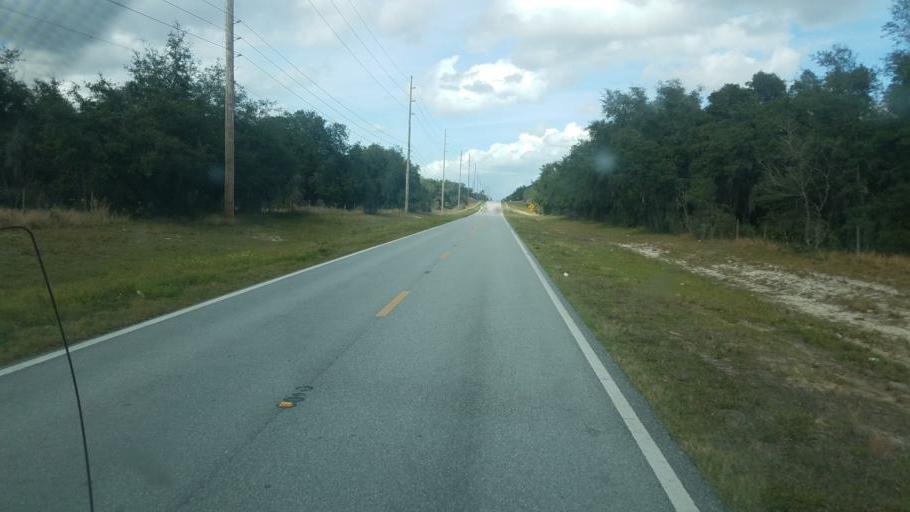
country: US
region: Florida
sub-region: Polk County
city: Lake Wales
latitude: 27.9478
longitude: -81.5379
